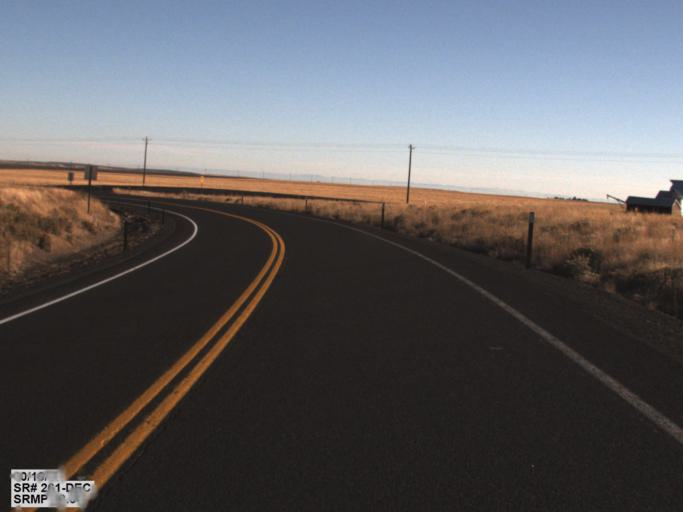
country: US
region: Washington
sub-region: Adams County
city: Ritzville
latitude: 46.9145
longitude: -118.3428
